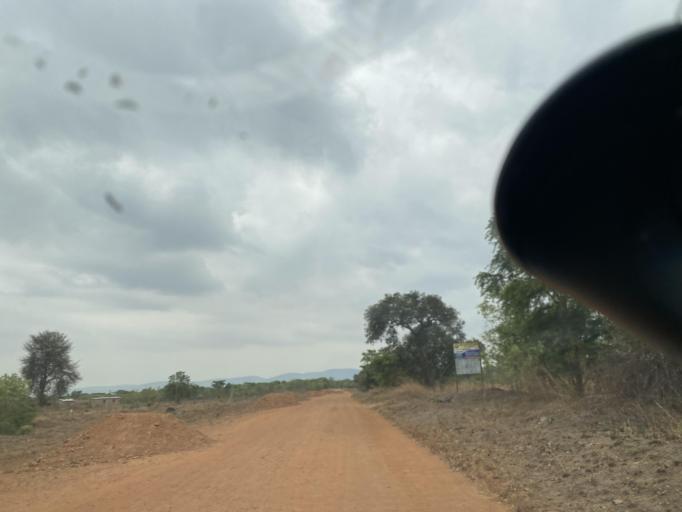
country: ZM
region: Lusaka
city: Chongwe
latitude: -15.2503
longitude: 28.7272
